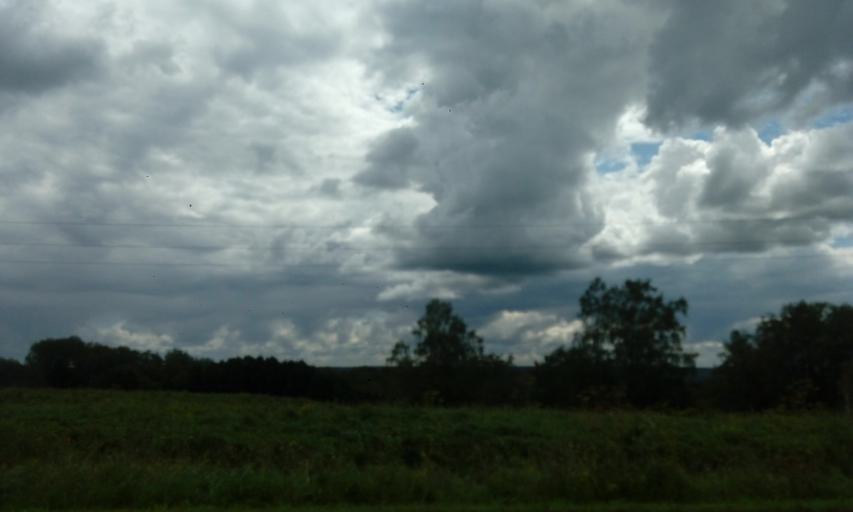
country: RU
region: Novosibirsk
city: Iskitim
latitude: 54.7877
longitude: 83.4264
